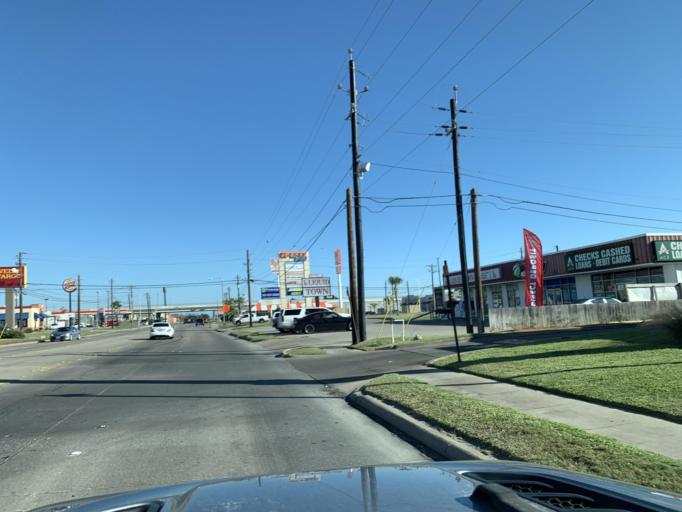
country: US
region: Texas
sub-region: Nueces County
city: Corpus Christi
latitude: 27.6665
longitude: -97.2835
